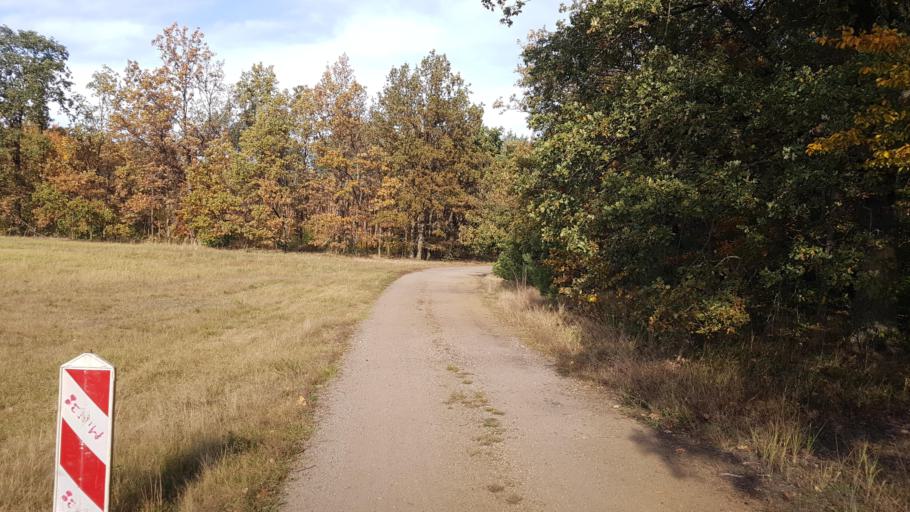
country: DE
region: Brandenburg
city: Tettau
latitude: 51.4316
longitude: 13.7570
